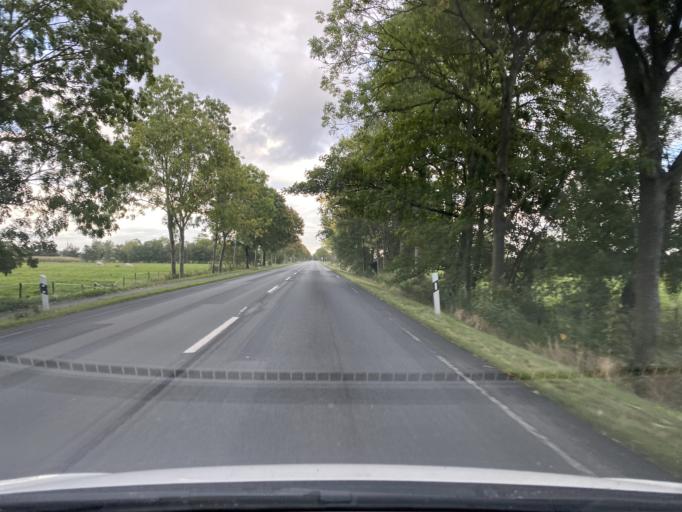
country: DE
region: Lower Saxony
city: Nordleda
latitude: 53.7998
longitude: 8.8441
